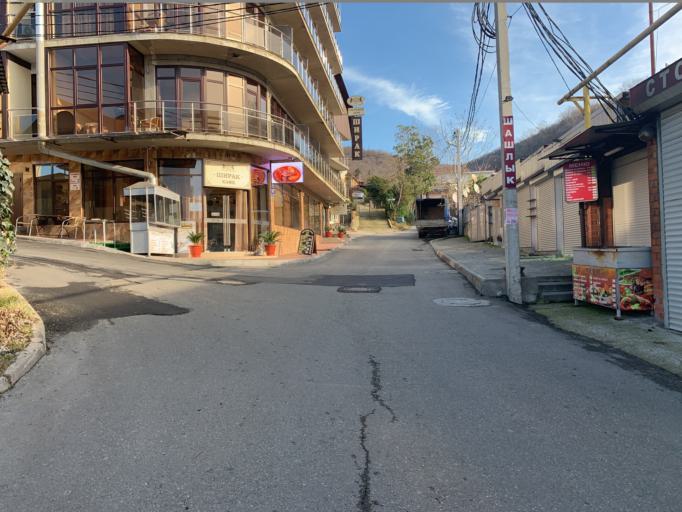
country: RU
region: Krasnodarskiy
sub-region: Sochi City
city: Lazarevskoye
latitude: 43.9207
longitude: 39.3194
